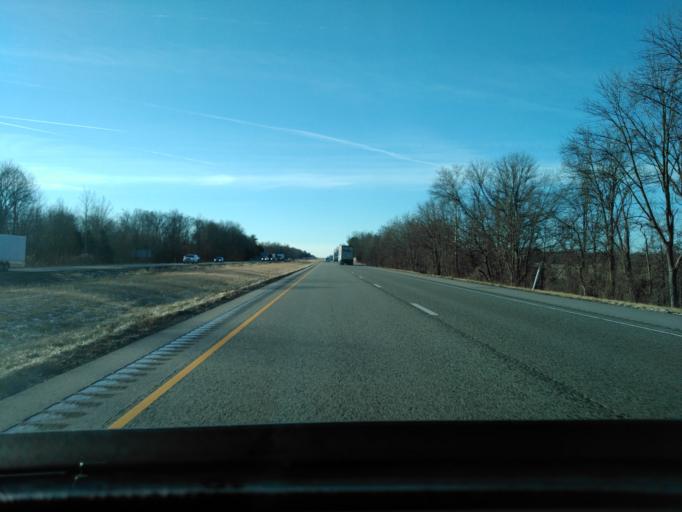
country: US
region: Illinois
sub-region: Franklin County
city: West Frankfort
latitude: 37.8736
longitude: -88.9418
